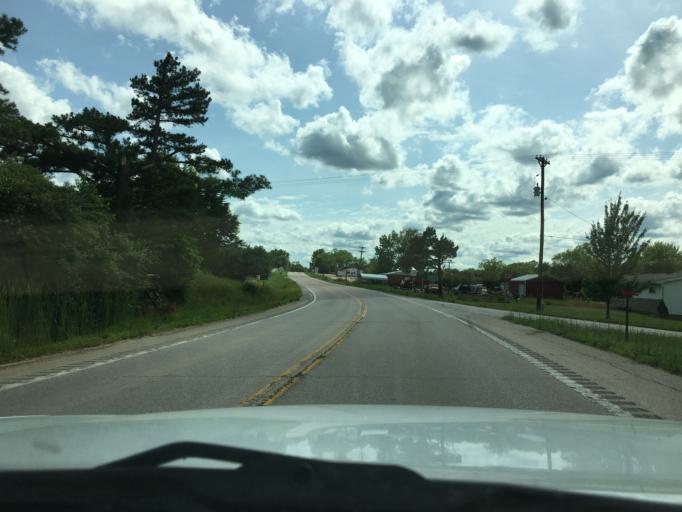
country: US
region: Missouri
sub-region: Franklin County
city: Gerald
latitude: 38.3933
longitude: -91.3665
